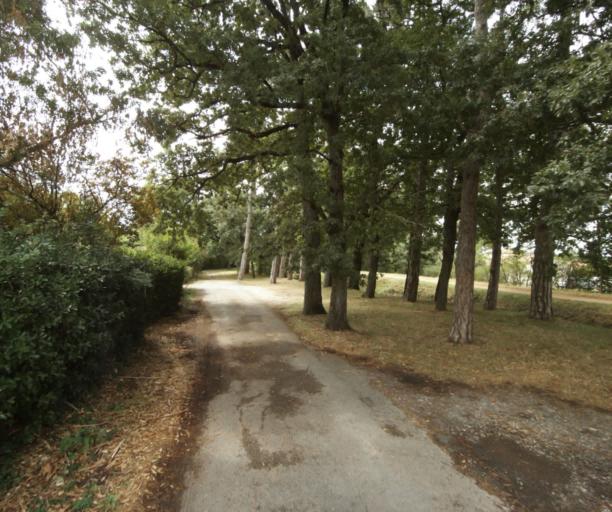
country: FR
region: Midi-Pyrenees
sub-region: Departement de la Haute-Garonne
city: Revel
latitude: 43.4515
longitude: 1.9966
